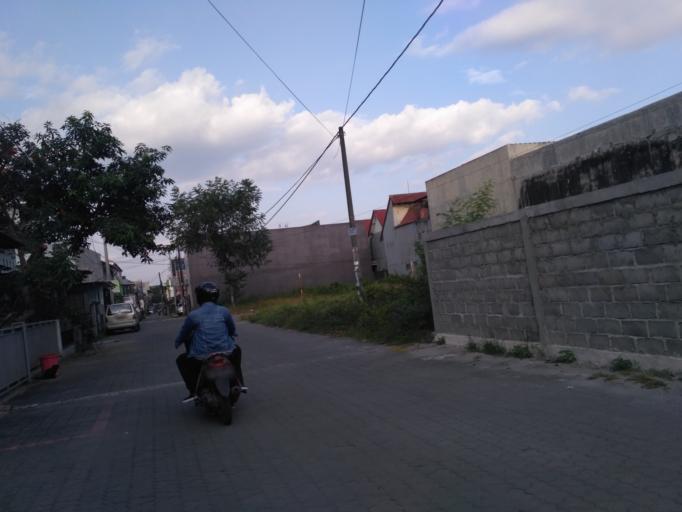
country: ID
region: Daerah Istimewa Yogyakarta
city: Depok
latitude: -7.7661
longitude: 110.4080
